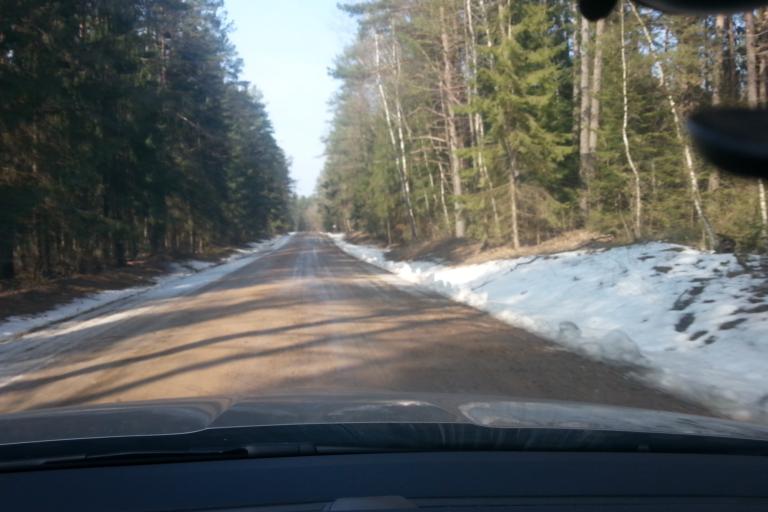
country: LT
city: Trakai
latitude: 54.5661
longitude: 24.9730
